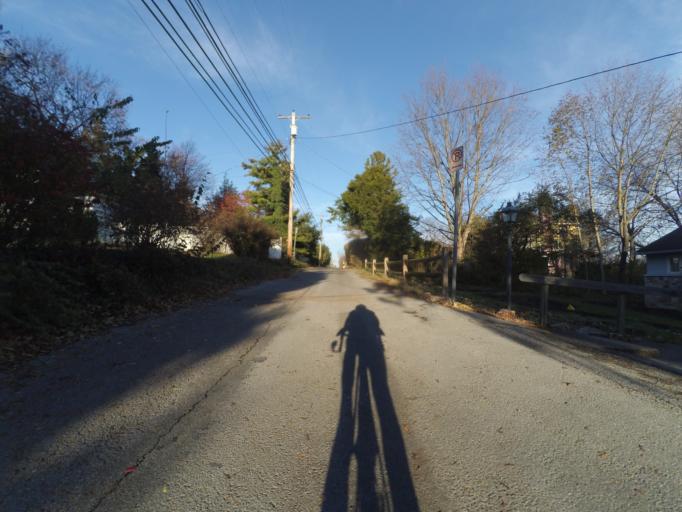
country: US
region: Pennsylvania
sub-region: Centre County
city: State College
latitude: 40.7864
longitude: -77.8615
